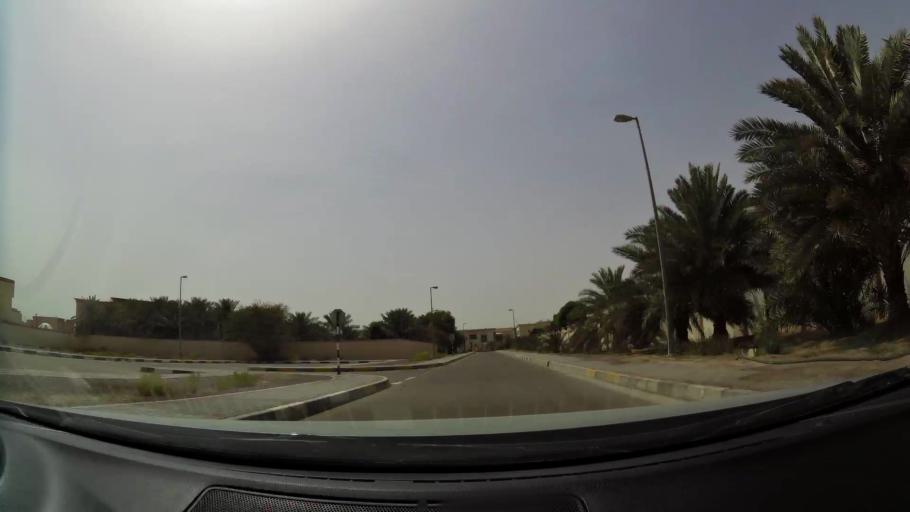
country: AE
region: Abu Dhabi
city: Al Ain
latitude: 24.1602
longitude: 55.6582
